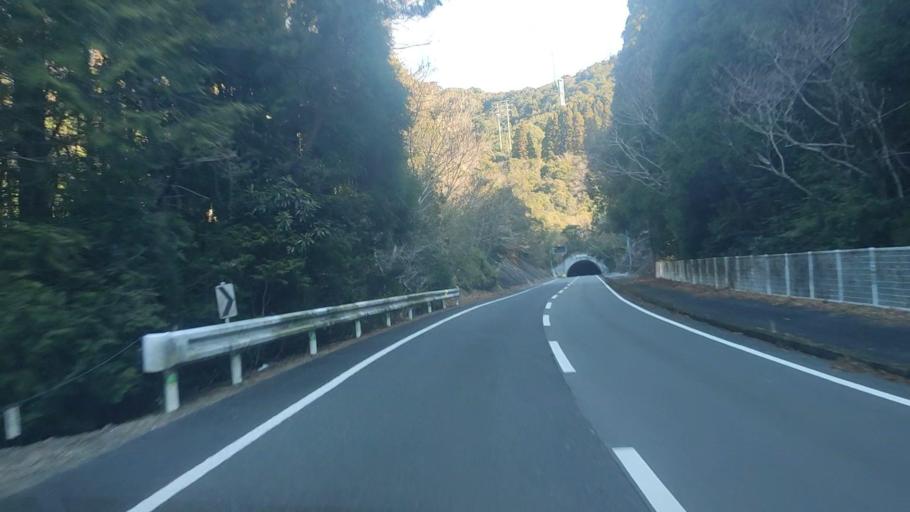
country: JP
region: Miyazaki
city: Nobeoka
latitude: 32.6692
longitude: 131.7667
